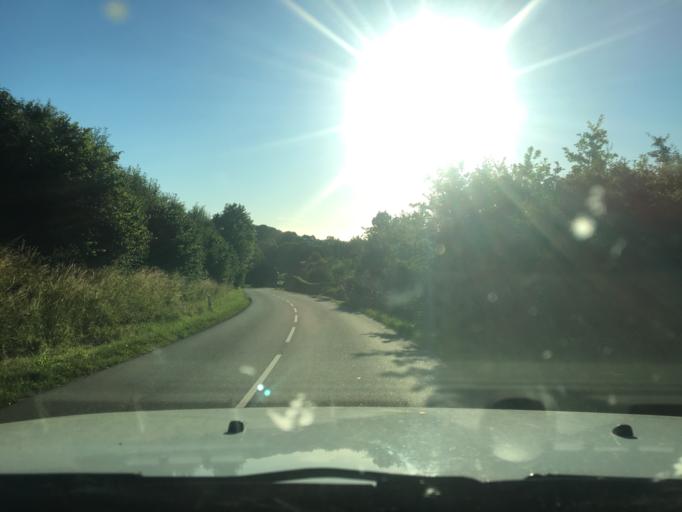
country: DK
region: Central Jutland
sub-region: Randers Kommune
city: Langa
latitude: 56.3937
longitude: 9.8831
